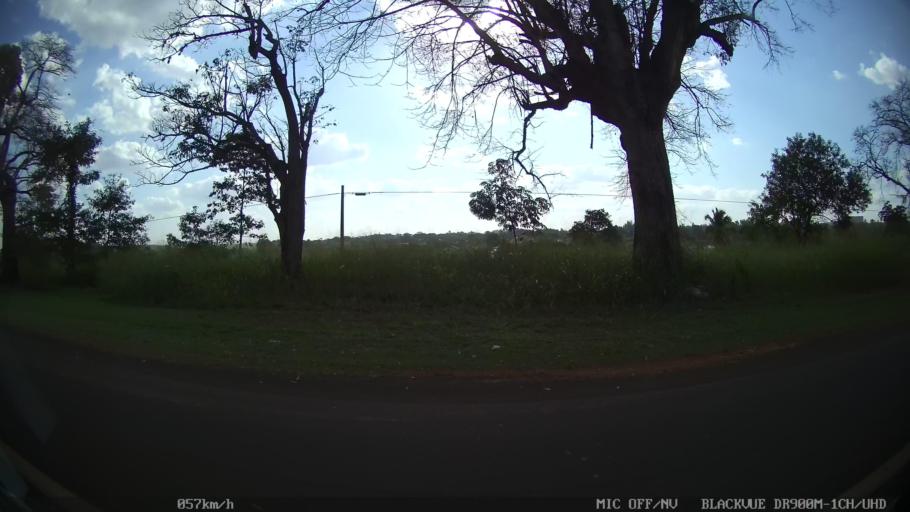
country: BR
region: Sao Paulo
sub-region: Ribeirao Preto
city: Ribeirao Preto
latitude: -21.1796
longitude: -47.8561
